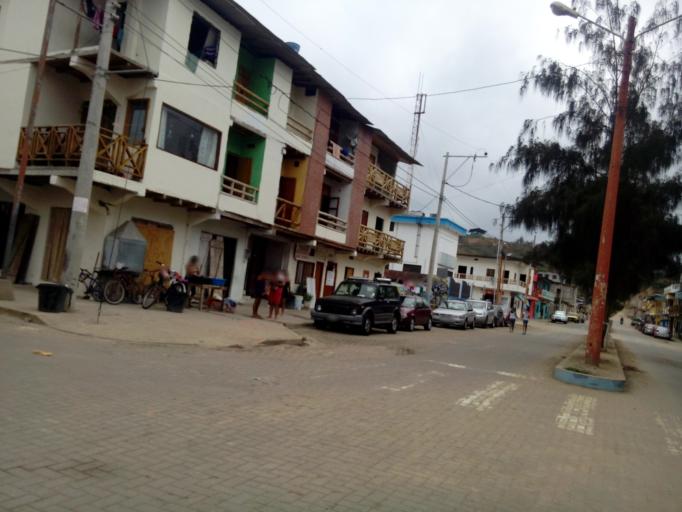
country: EC
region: Santa Elena
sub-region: Canton Santa Elena
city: Santa Elena
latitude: -1.8301
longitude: -80.7522
